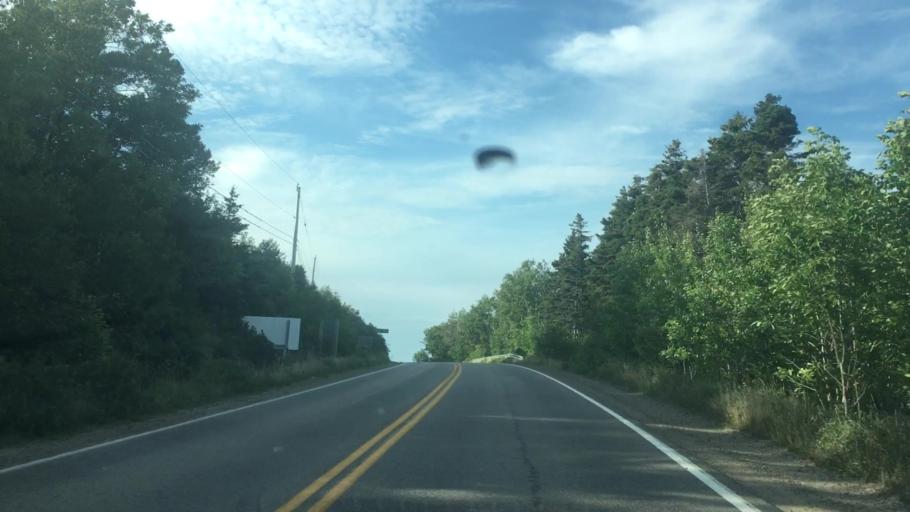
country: CA
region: Nova Scotia
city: Sydney Mines
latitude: 46.8240
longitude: -60.8002
